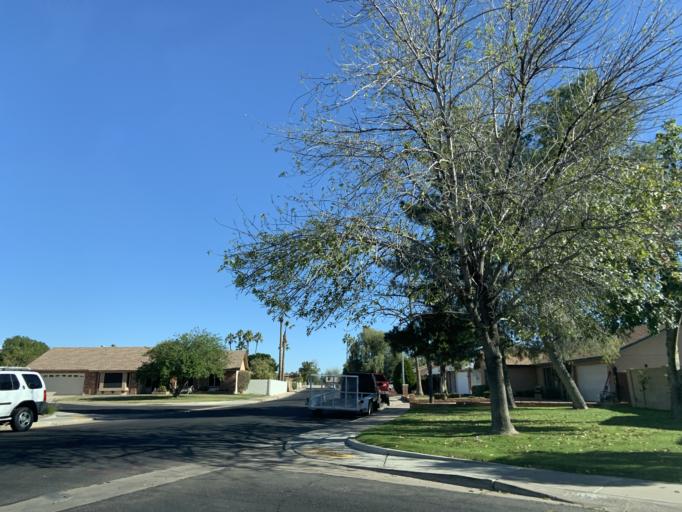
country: US
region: Arizona
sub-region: Maricopa County
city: San Carlos
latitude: 33.3737
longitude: -111.8639
